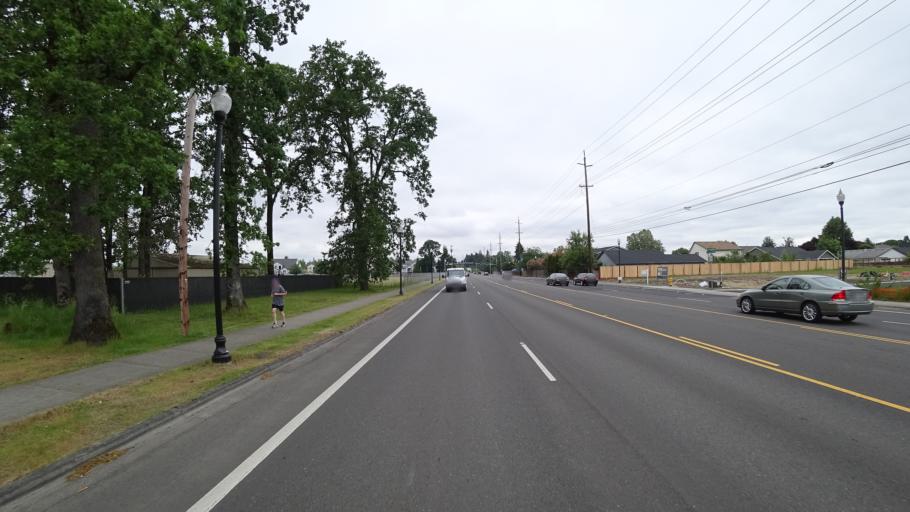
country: US
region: Oregon
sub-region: Washington County
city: Aloha
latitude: 45.5105
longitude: -122.9021
